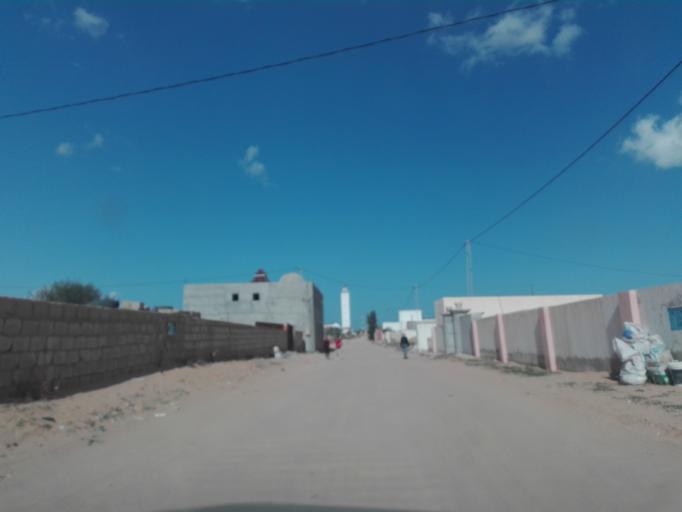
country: TN
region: Madanin
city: Bin Qirdan
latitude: 33.1579
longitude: 11.1943
